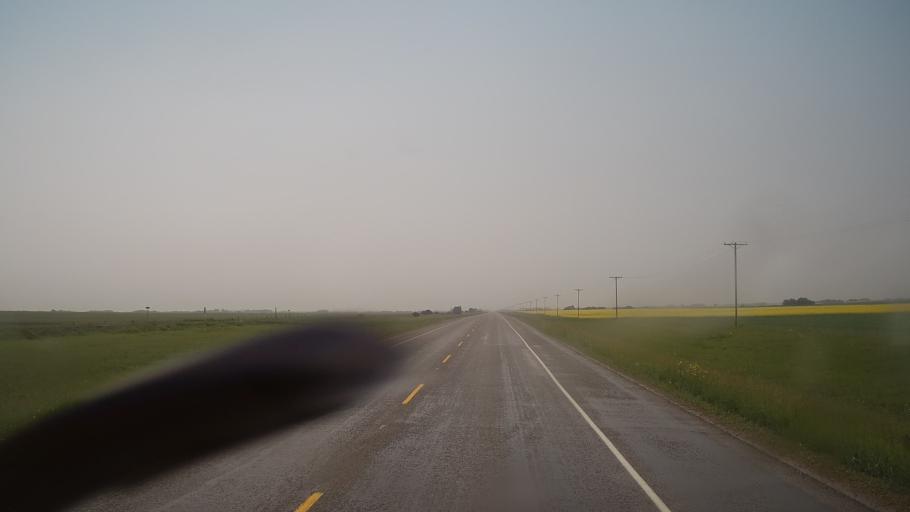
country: CA
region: Saskatchewan
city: Biggar
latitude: 52.1470
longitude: -108.2147
